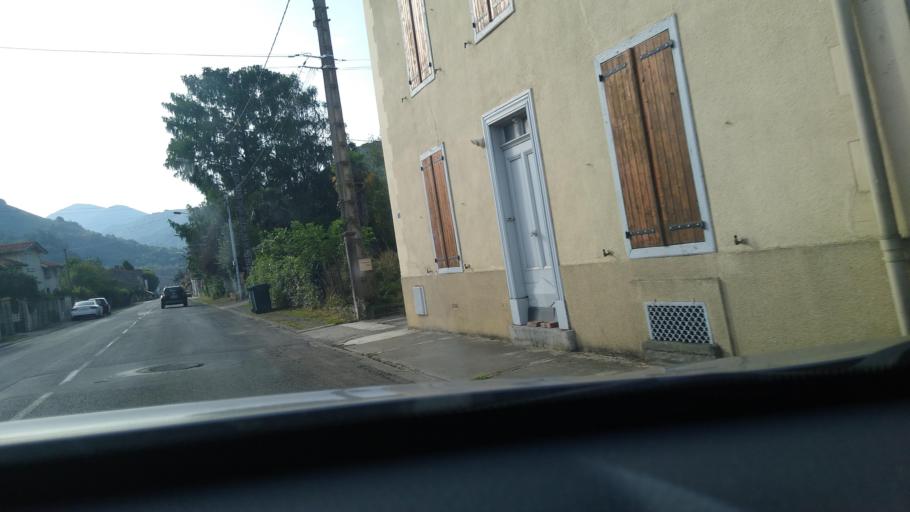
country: FR
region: Midi-Pyrenees
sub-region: Departement de l'Ariege
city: Saint-Girons
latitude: 42.9702
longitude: 1.1602
